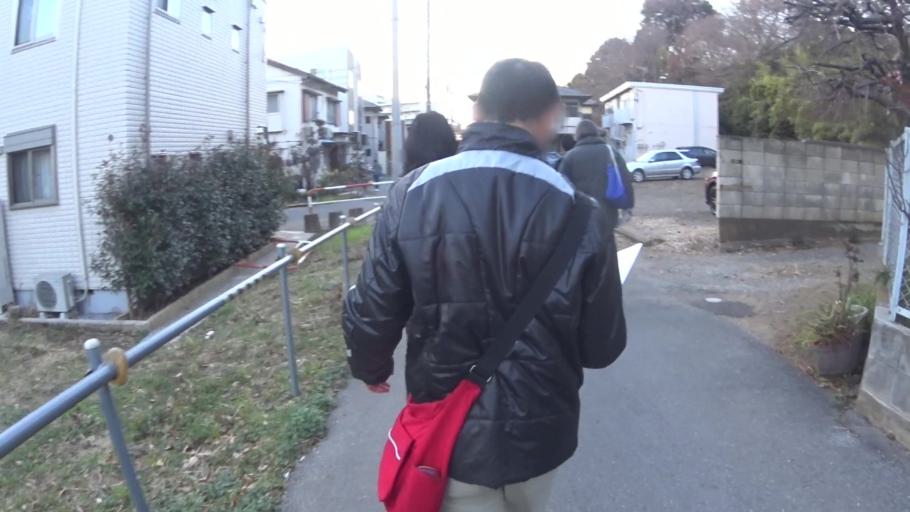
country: JP
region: Saitama
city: Shimotoda
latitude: 35.8461
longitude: 139.6786
